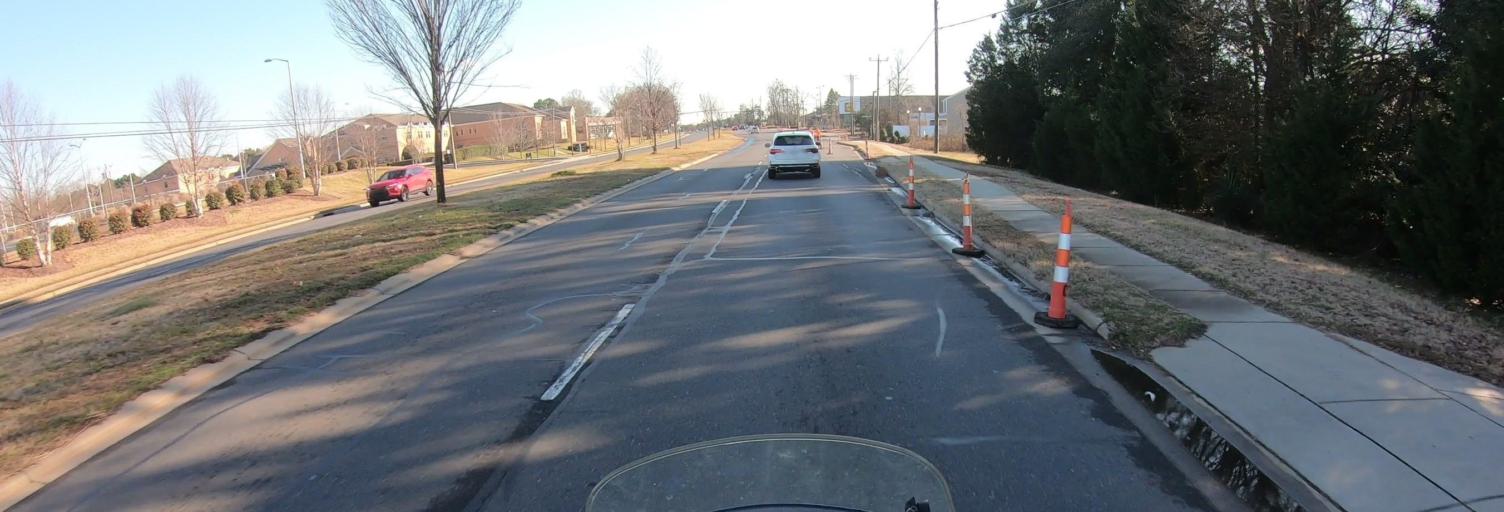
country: US
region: South Carolina
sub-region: York County
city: Lake Wylie
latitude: 35.1141
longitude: -80.9652
